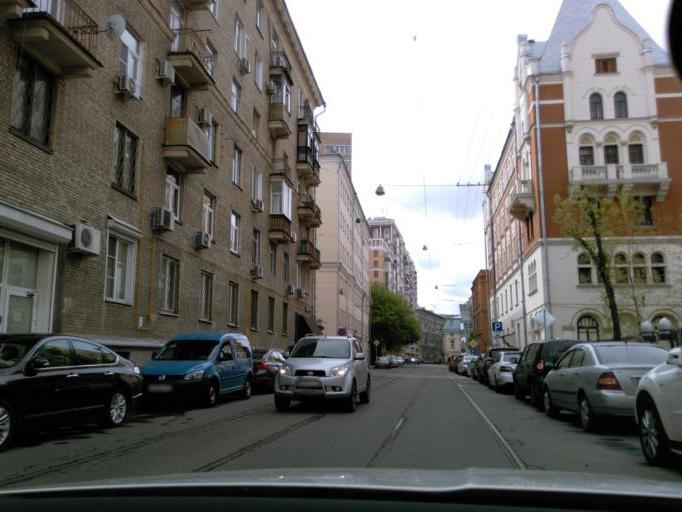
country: RU
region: Moscow
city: Mar'ina Roshcha
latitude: 55.7874
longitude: 37.6330
